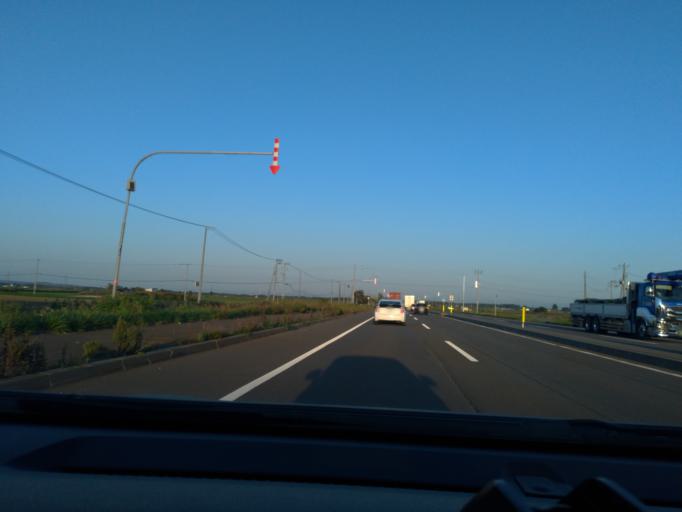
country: JP
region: Hokkaido
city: Tobetsu
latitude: 43.1786
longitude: 141.4547
